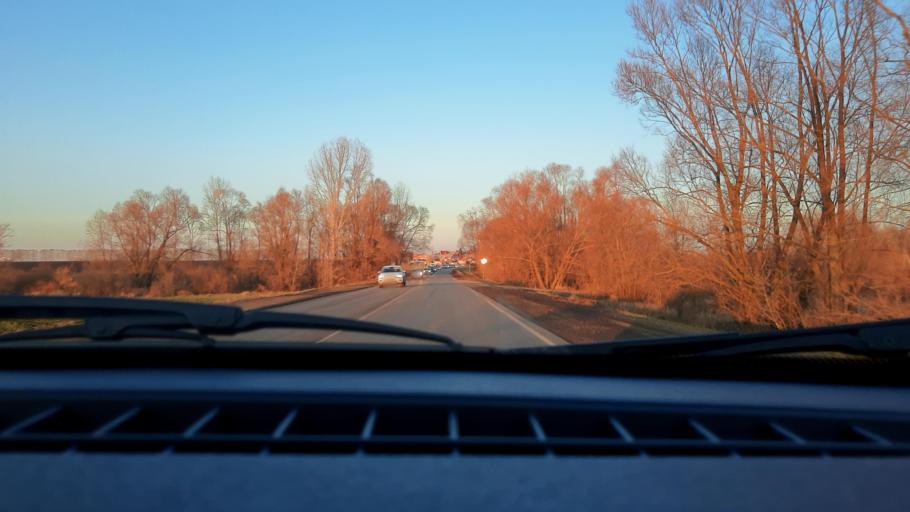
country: RU
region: Bashkortostan
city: Ufa
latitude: 54.8151
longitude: 55.9782
